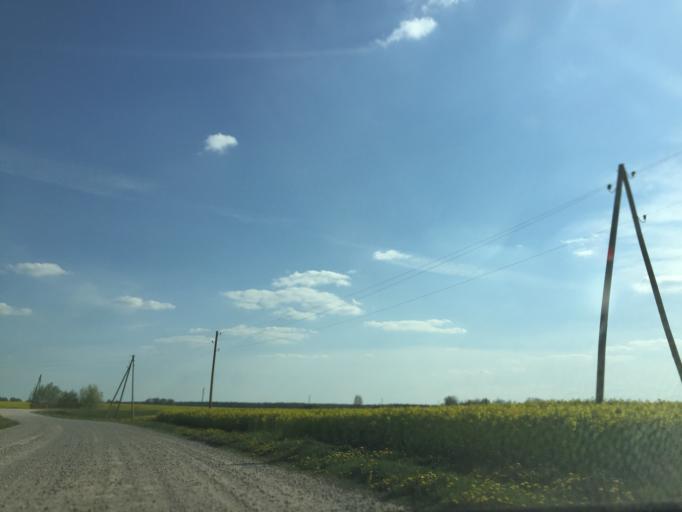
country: LV
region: Bauskas Rajons
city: Bauska
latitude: 56.4875
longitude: 24.3290
